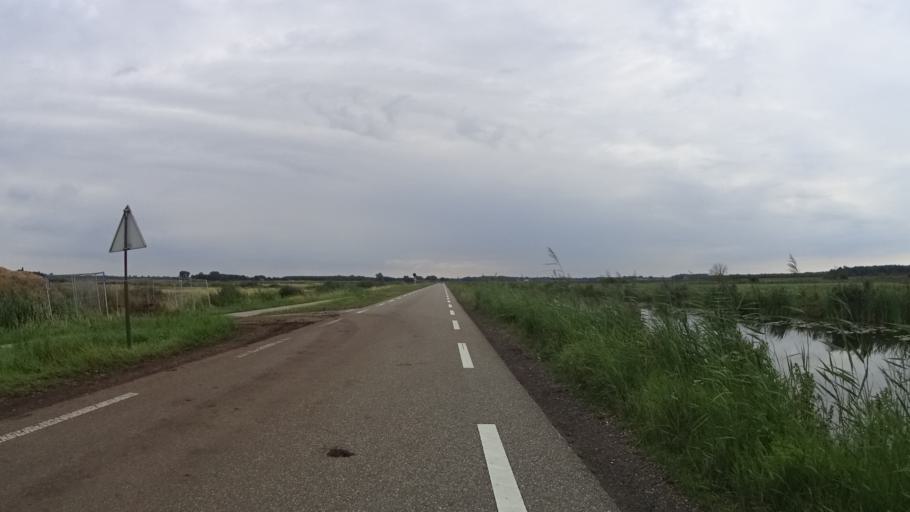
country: NL
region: Groningen
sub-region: Gemeente Slochteren
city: Slochteren
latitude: 53.2309
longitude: 6.7589
